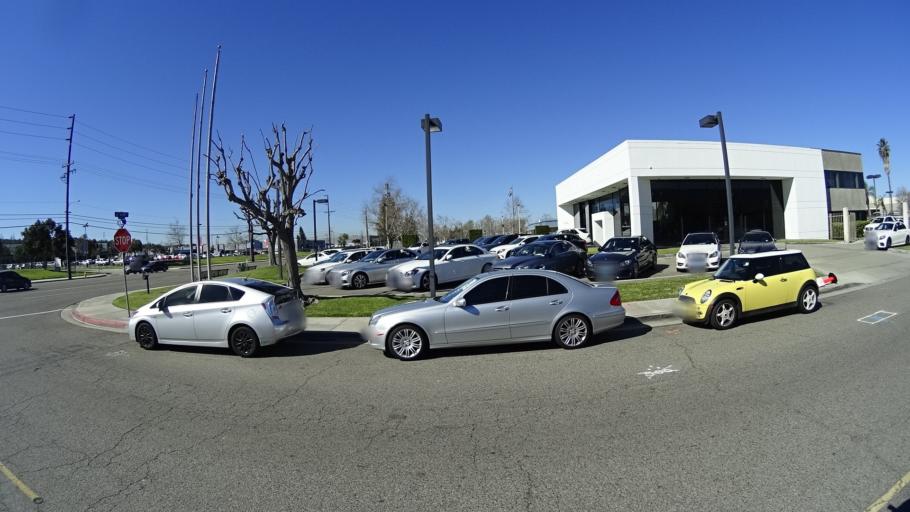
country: US
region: California
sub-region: Orange County
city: Yorba Linda
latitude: 33.8598
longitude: -117.7990
